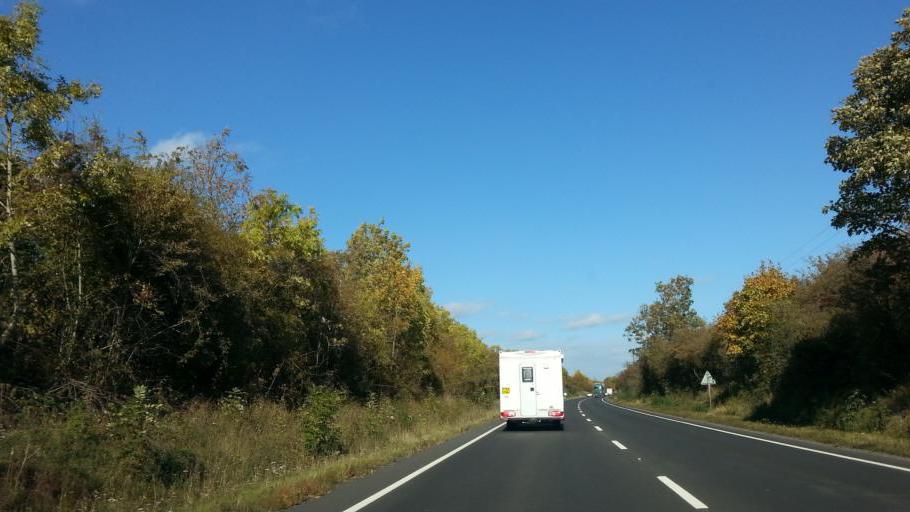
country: GB
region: England
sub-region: Northamptonshire
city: Oundle
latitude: 52.4591
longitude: -0.4624
